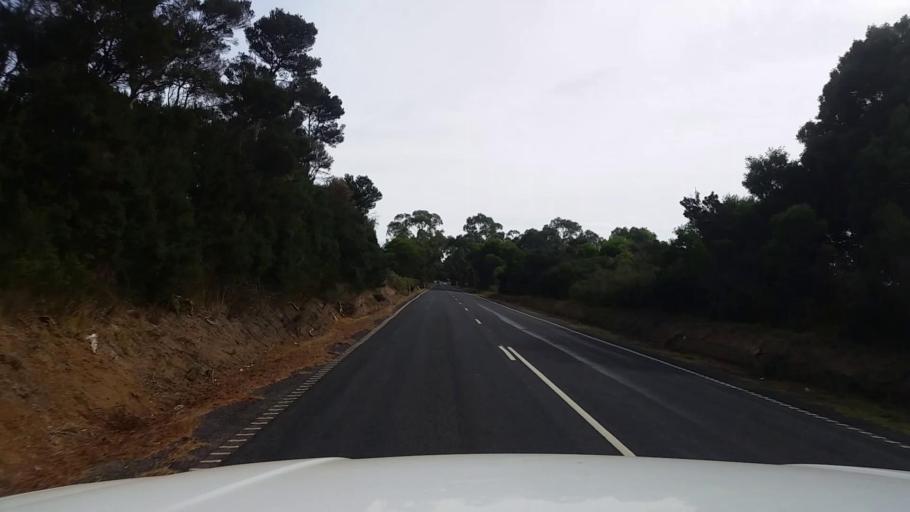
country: AU
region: Victoria
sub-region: Mornington Peninsula
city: Merricks
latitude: -38.3160
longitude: 145.0880
